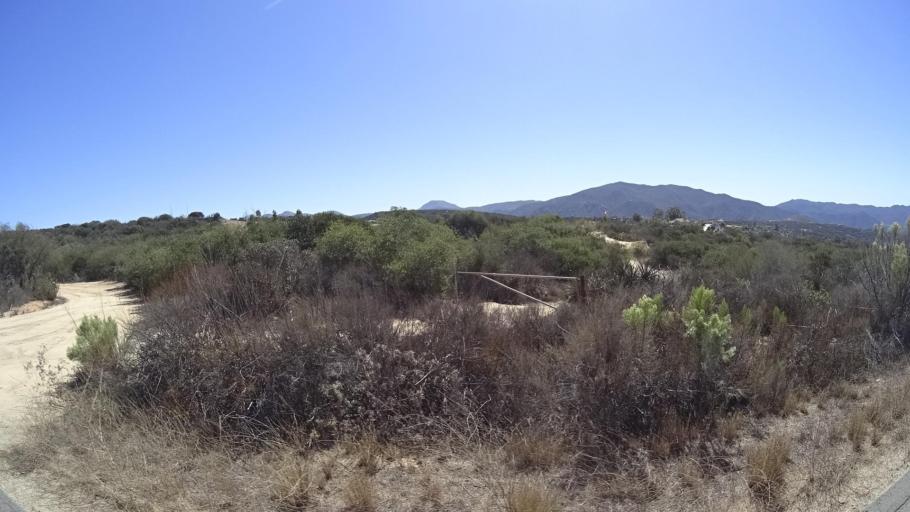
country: US
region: California
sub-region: San Diego County
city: Harbison Canyon
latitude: 32.7953
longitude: -116.8015
